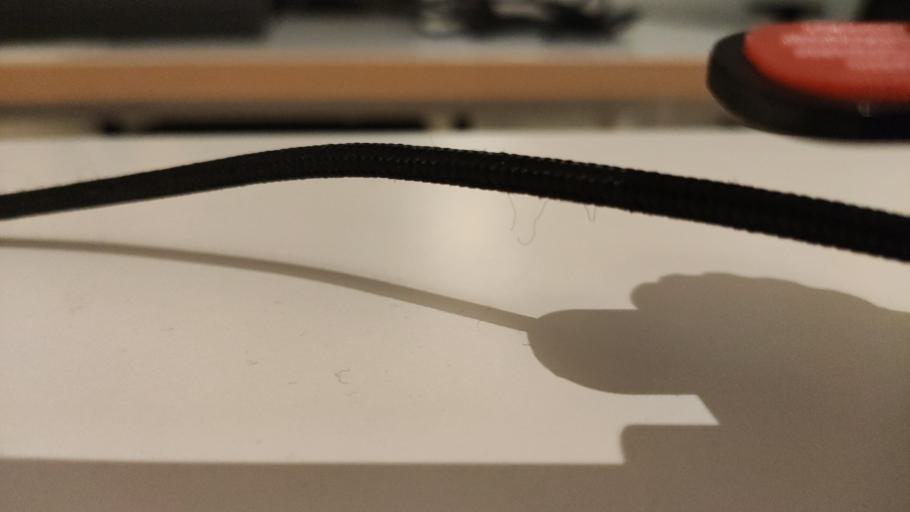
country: RU
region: Moskovskaya
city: Malino
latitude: 55.1114
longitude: 38.1596
